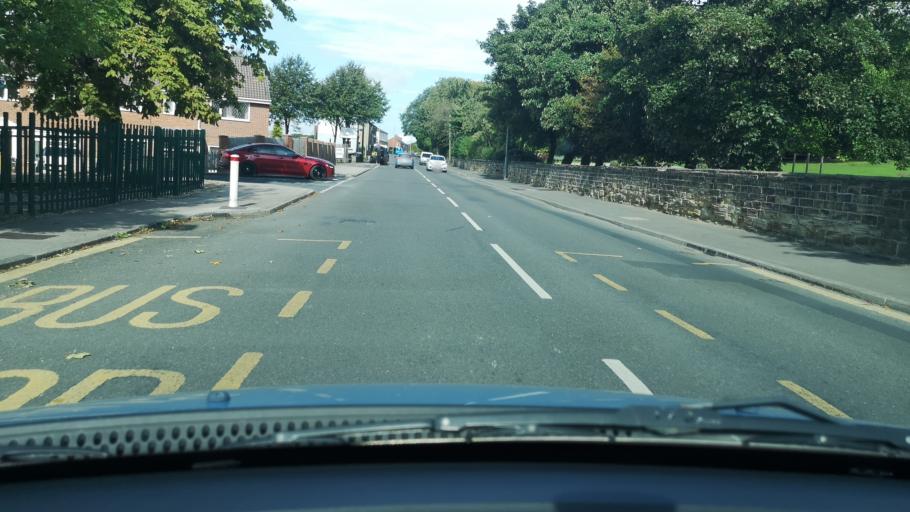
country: GB
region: England
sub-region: City and Borough of Wakefield
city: Ossett
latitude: 53.6716
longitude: -1.5755
